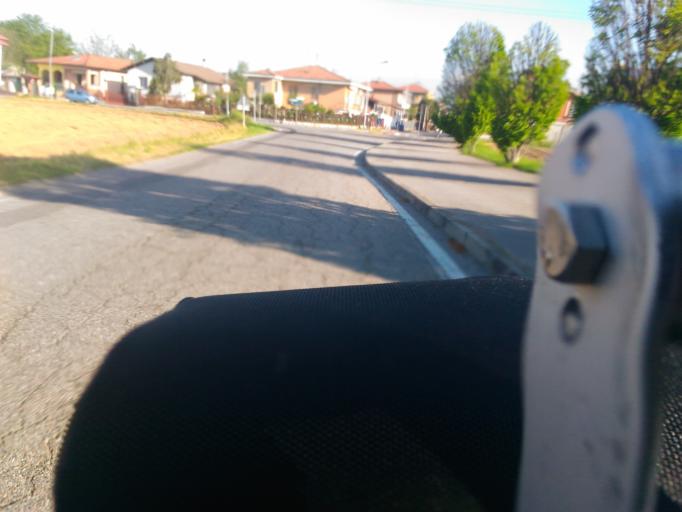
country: IT
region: Lombardy
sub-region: Citta metropolitana di Milano
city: Vizzolo Predabissi
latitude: 45.3559
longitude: 9.3518
